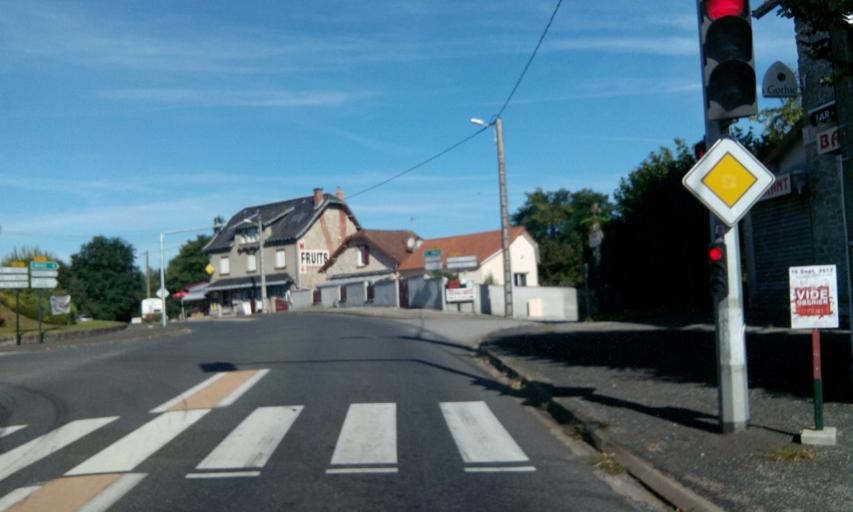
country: FR
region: Limousin
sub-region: Departement de la Haute-Vienne
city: Saint-Just-le-Martel
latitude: 45.8486
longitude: 1.4301
